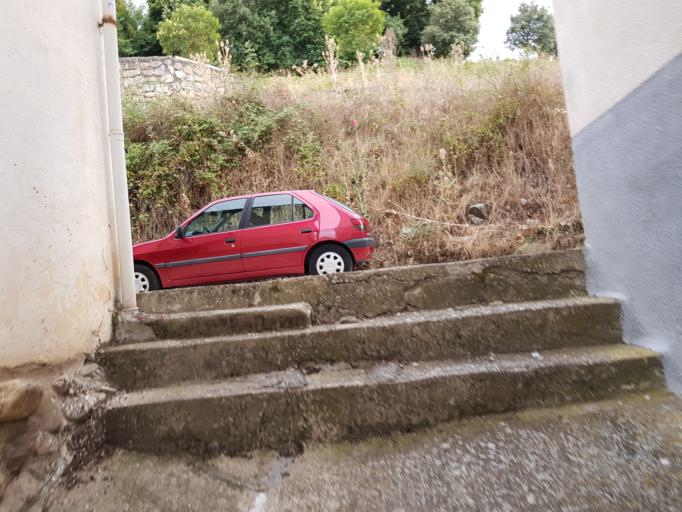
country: ES
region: La Rioja
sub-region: Provincia de La Rioja
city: Torrecilla en Cameros
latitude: 42.2558
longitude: -2.6326
